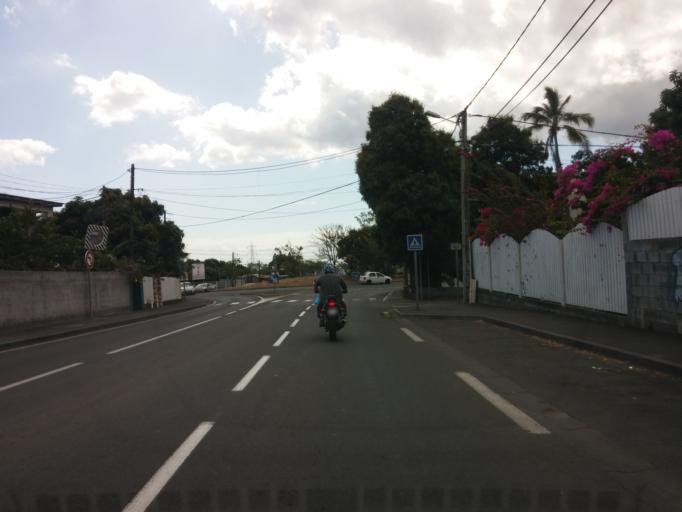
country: RE
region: Reunion
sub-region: Reunion
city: La Possession
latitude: -20.9463
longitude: 55.3277
